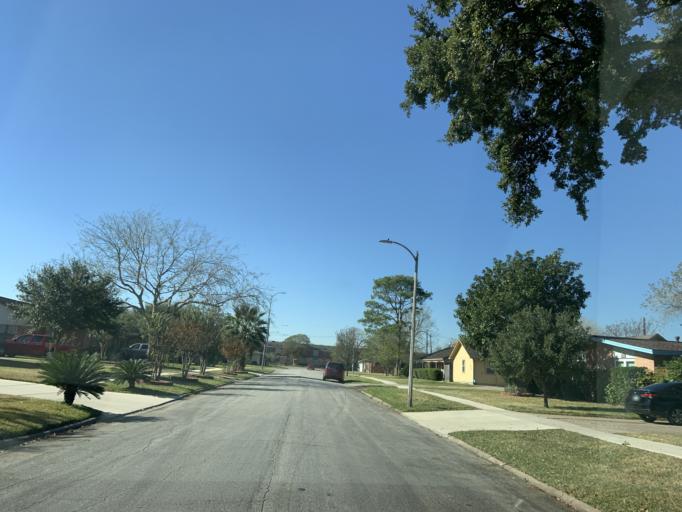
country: US
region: Texas
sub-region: Harris County
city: Bellaire
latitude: 29.6845
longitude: -95.5071
